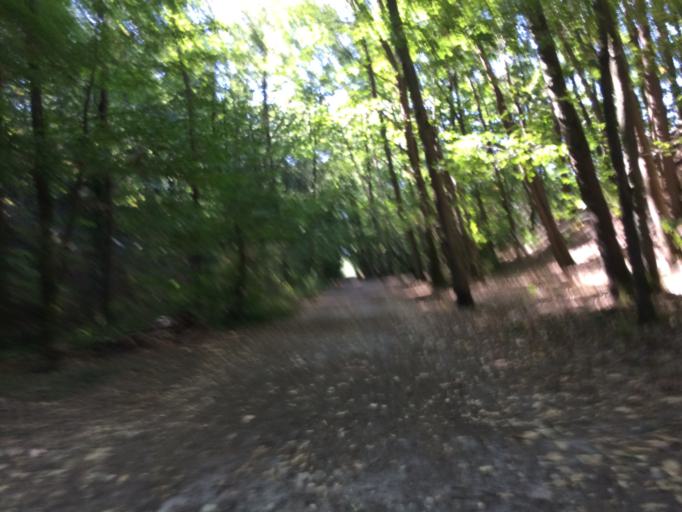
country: FR
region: Ile-de-France
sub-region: Departement de l'Essonne
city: Les Ulis
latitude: 48.6819
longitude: 2.1543
